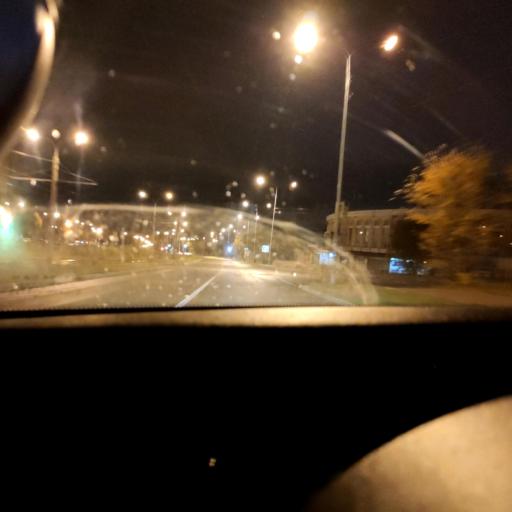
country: RU
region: Samara
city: Samara
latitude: 53.2518
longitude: 50.2467
